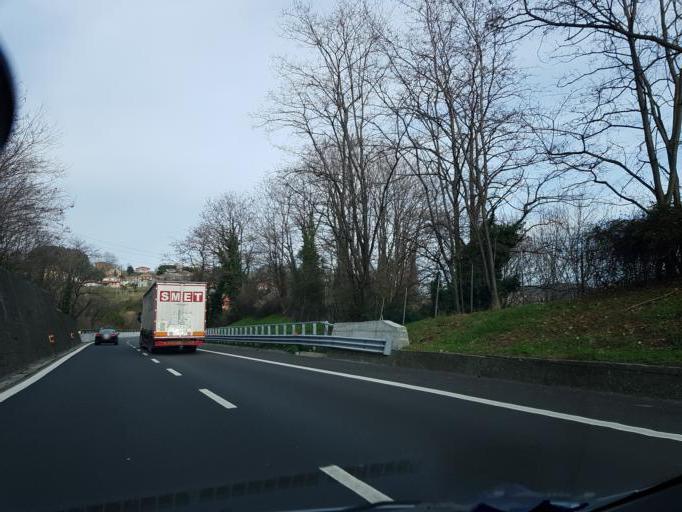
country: IT
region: Liguria
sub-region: Provincia di Genova
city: Pedemonte
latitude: 44.4948
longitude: 8.9170
